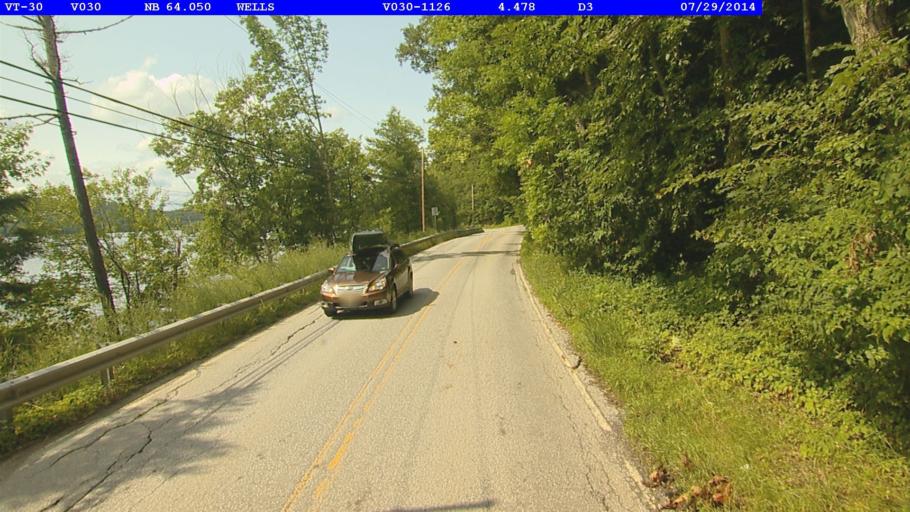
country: US
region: Vermont
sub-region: Rutland County
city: Poultney
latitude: 43.4554
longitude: -73.2049
